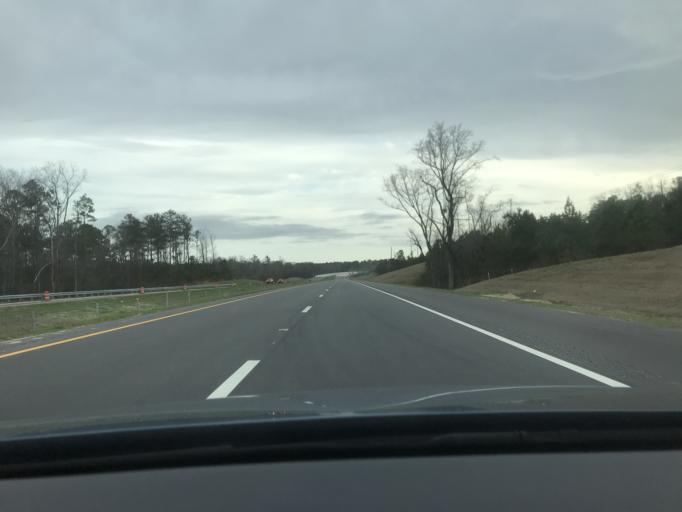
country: US
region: North Carolina
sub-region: Cumberland County
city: Fort Bragg
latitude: 35.0868
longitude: -79.0246
